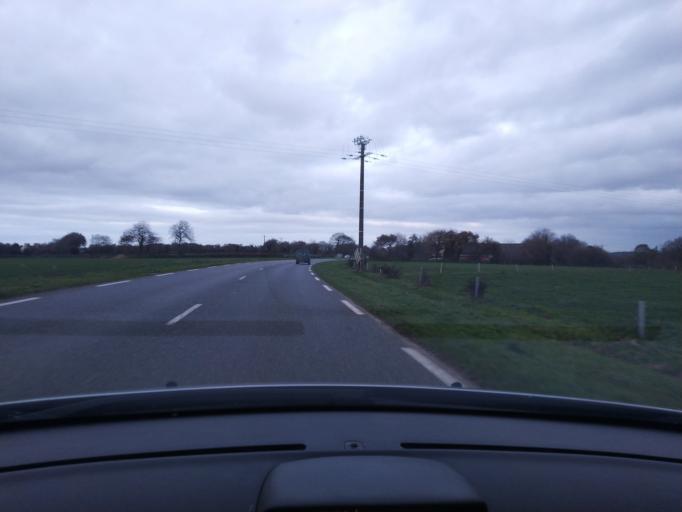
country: FR
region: Brittany
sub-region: Departement des Cotes-d'Armor
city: Plouaret
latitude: 48.5979
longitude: -3.4916
